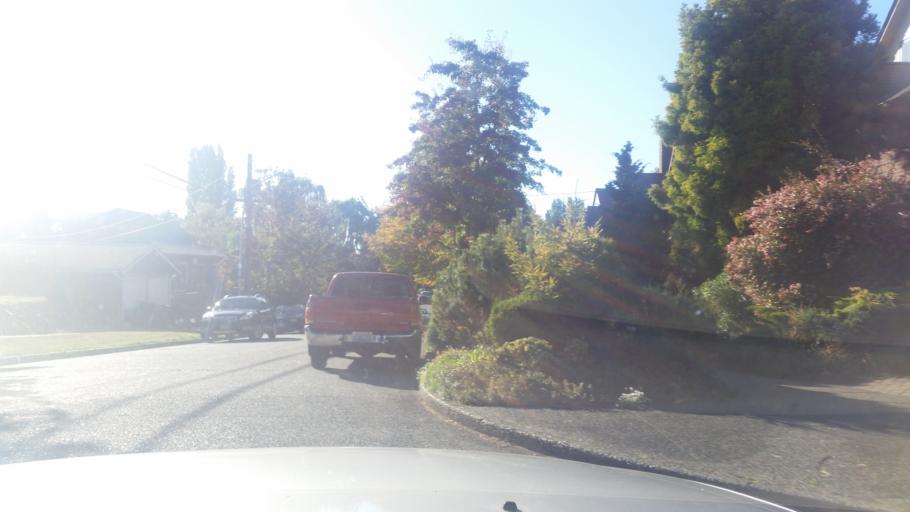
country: US
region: Washington
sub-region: King County
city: Shoreline
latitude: 47.6888
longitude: -122.3705
